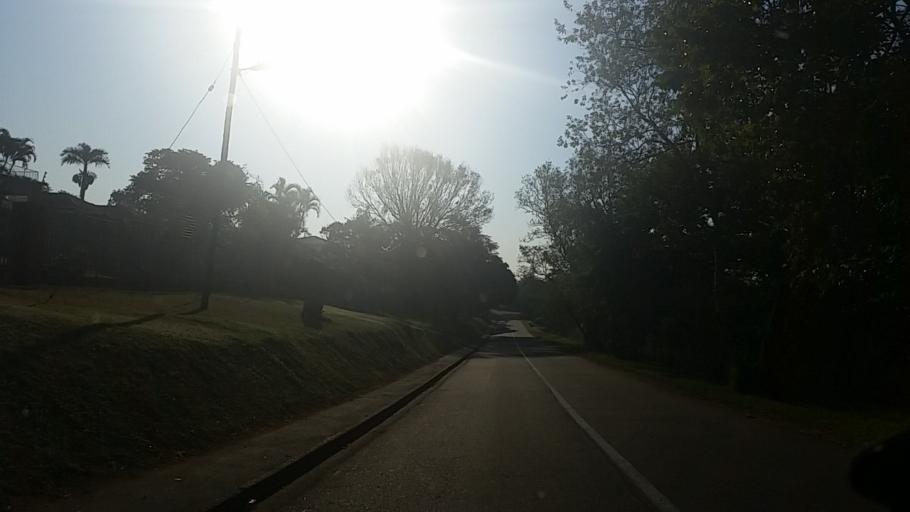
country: ZA
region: KwaZulu-Natal
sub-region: eThekwini Metropolitan Municipality
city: Berea
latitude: -29.8440
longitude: 30.9248
